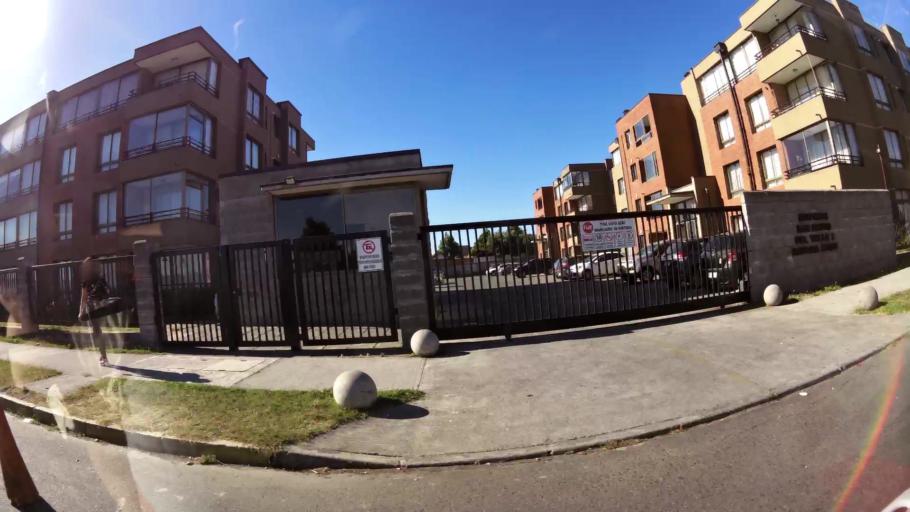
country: CL
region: Biobio
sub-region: Provincia de Concepcion
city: Concepcion
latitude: -36.8426
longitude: -73.1171
